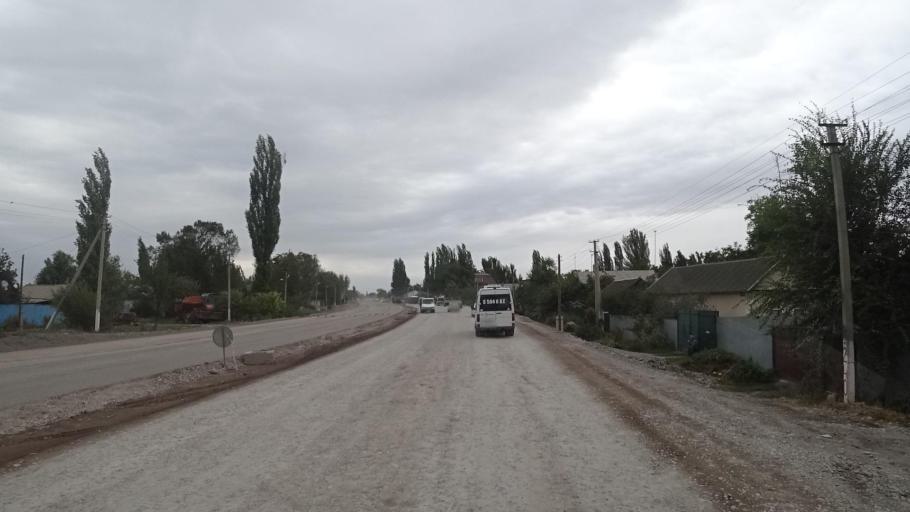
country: KG
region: Chuy
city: Belovodskoye
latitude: 42.8347
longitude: 74.1285
